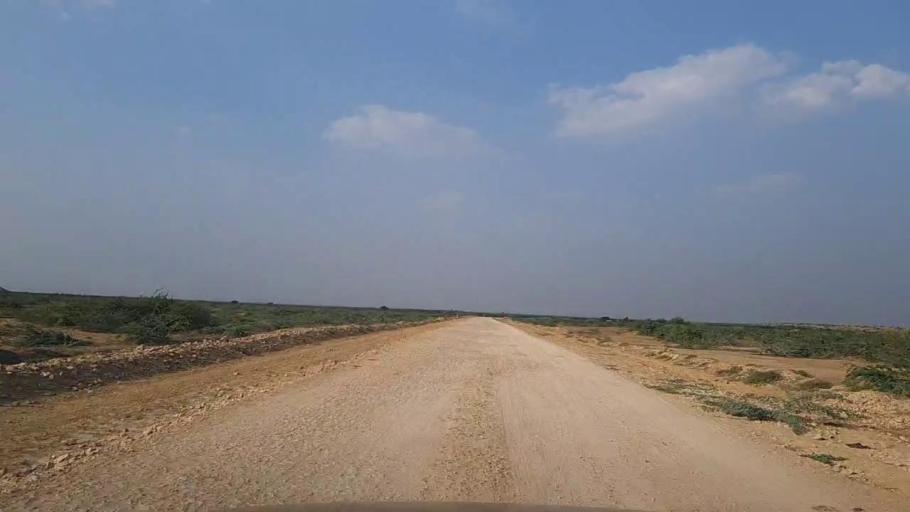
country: PK
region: Sindh
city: Gharo
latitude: 24.8123
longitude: 67.7419
